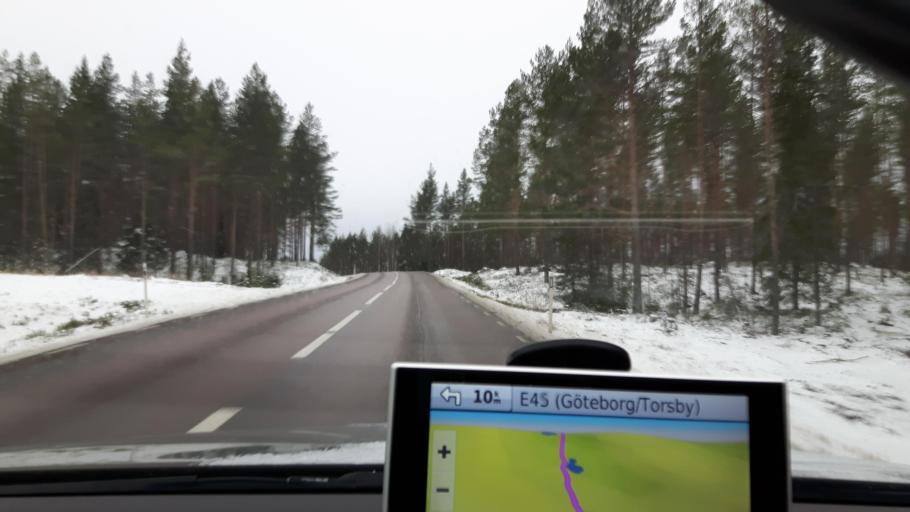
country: SE
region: Vaermland
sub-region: Torsby Kommun
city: Torsby
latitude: 60.3444
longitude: 13.1575
